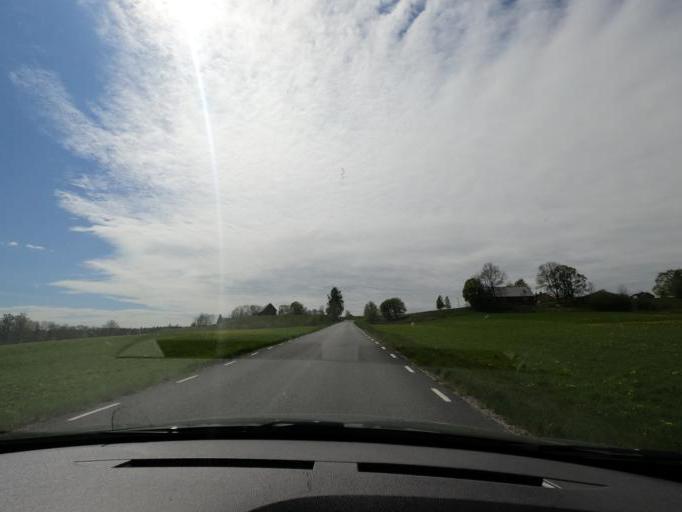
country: SE
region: Joenkoeping
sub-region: Varnamo Kommun
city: Bredaryd
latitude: 57.1272
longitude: 13.6821
